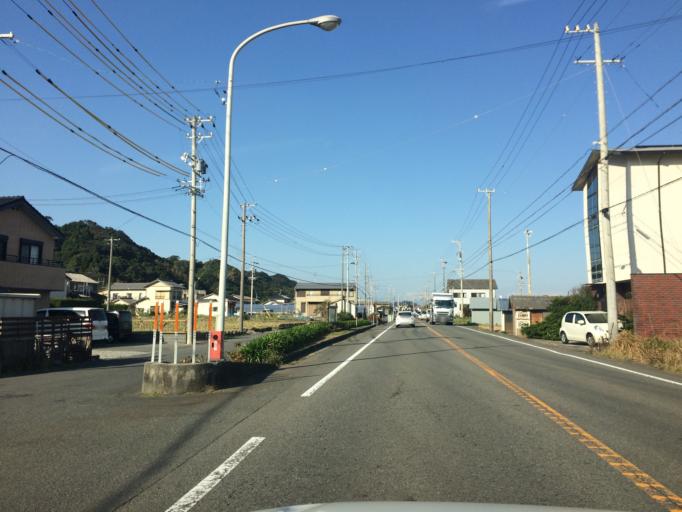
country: JP
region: Shizuoka
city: Sagara
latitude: 34.7045
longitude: 138.2128
